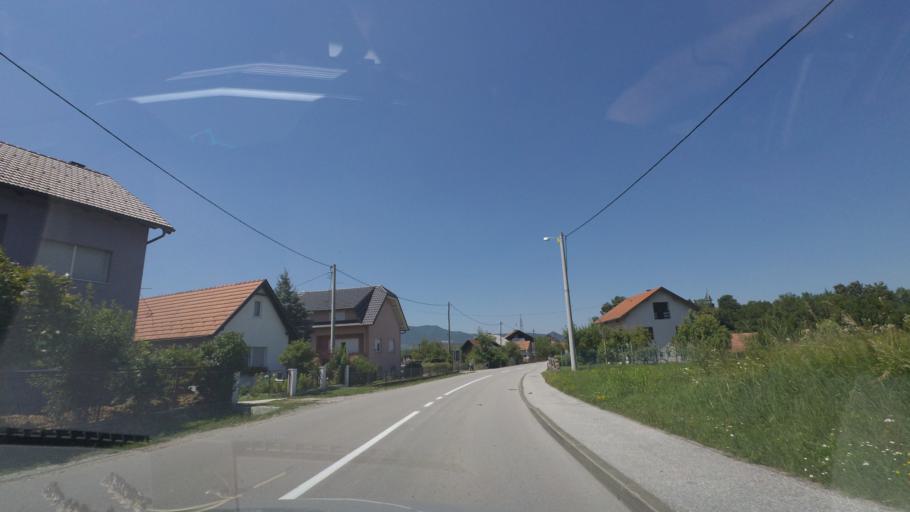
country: HR
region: Grad Zagreb
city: Horvati
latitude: 45.6862
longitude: 15.7470
